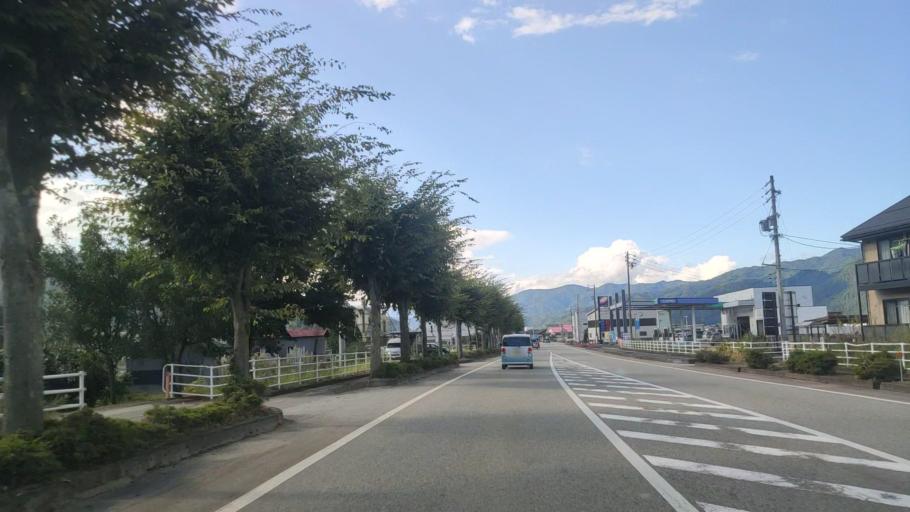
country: JP
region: Gifu
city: Takayama
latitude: 36.2233
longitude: 137.1902
